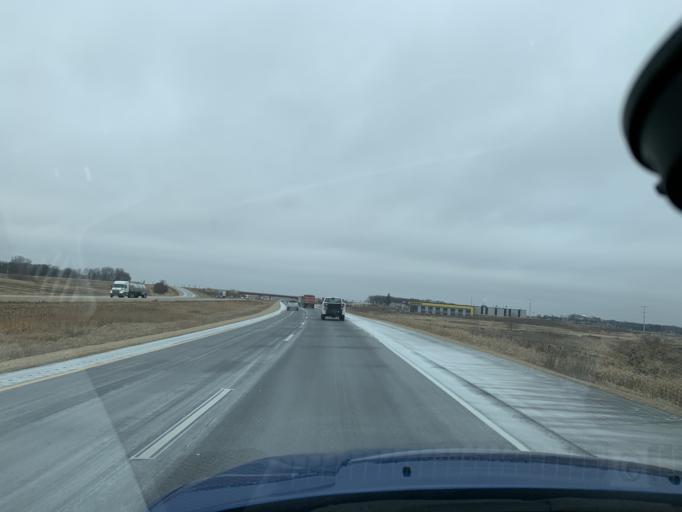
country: US
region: Wisconsin
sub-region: Columbia County
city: Columbus
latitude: 43.3113
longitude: -89.0457
